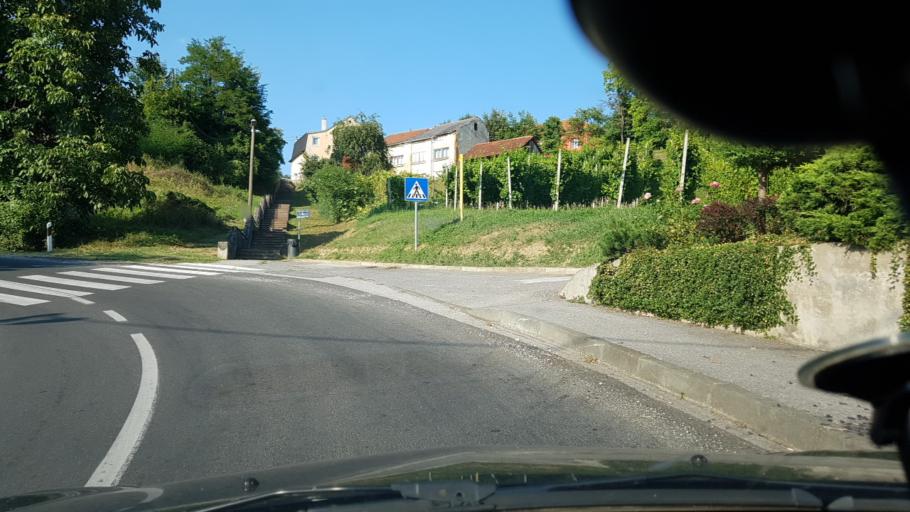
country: SI
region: Bistrica ob Sotli
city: Bistrica ob Sotli
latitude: 46.0474
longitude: 15.7374
